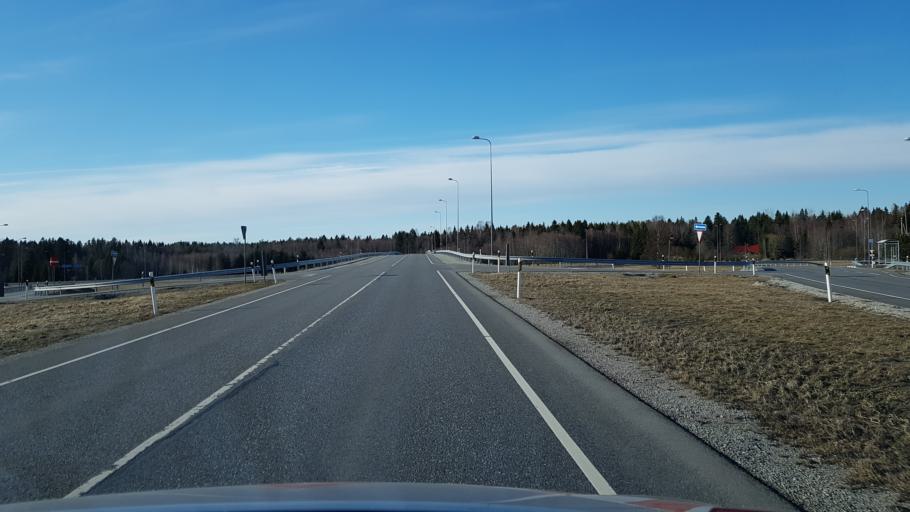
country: EE
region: Laeaene-Virumaa
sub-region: Tapa vald
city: Tapa
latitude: 59.4527
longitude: 25.9446
